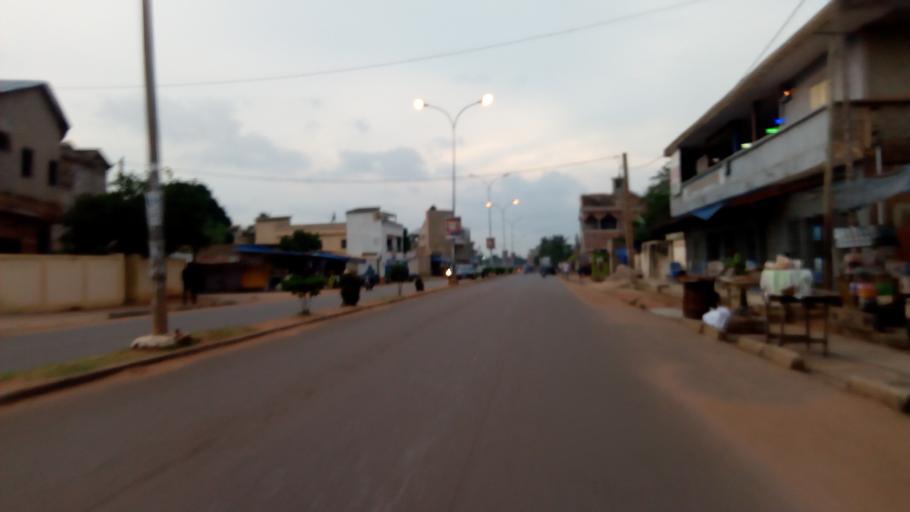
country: TG
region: Maritime
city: Lome
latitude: 6.2164
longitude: 1.2026
